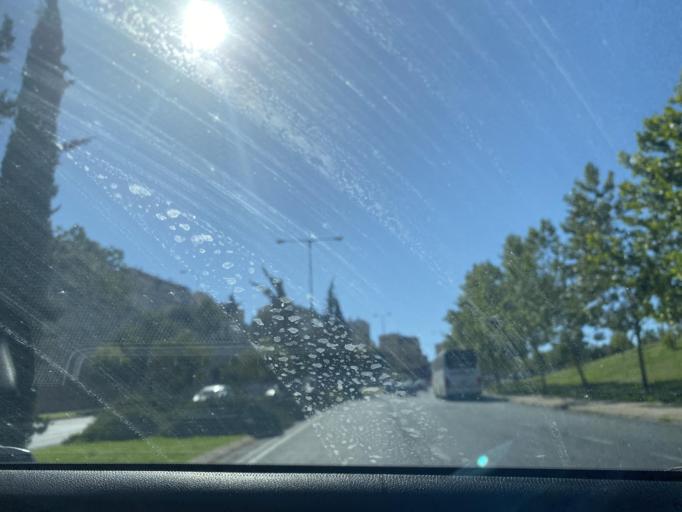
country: PS
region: West Bank
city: Bayt Iksa
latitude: 31.8199
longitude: 35.1915
